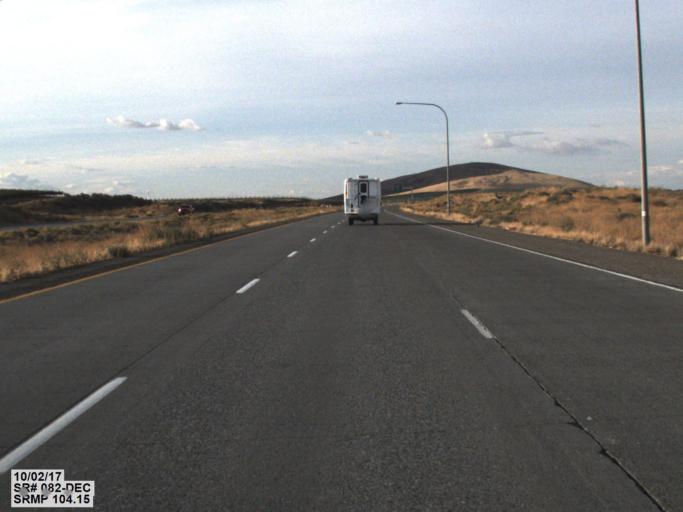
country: US
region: Washington
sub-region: Benton County
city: West Richland
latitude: 46.2222
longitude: -119.3507
